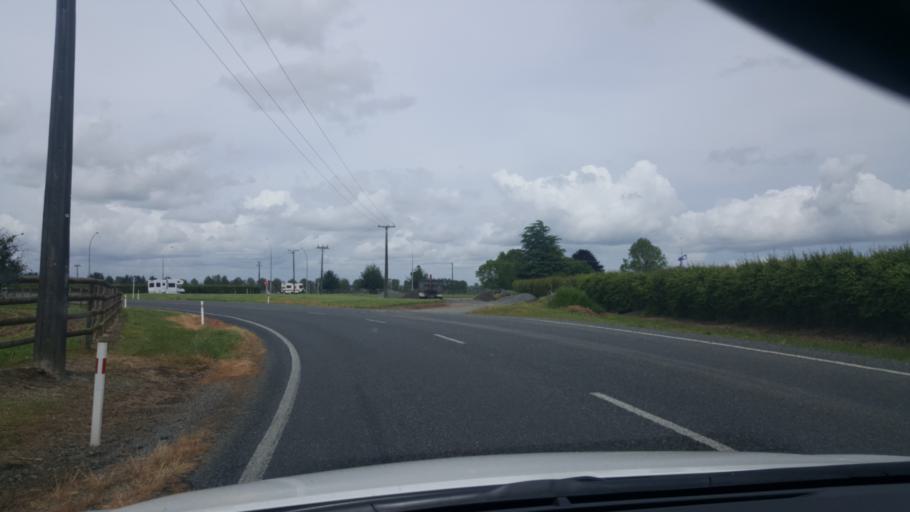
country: NZ
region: Waikato
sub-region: Matamata-Piako District
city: Matamata
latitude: -37.8822
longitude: 175.7314
